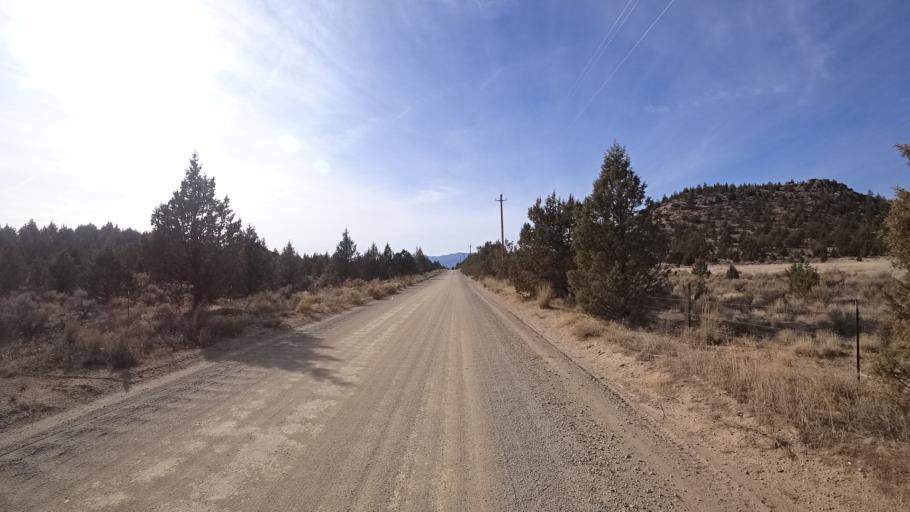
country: US
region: California
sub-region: Siskiyou County
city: Montague
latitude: 41.5807
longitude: -122.4556
